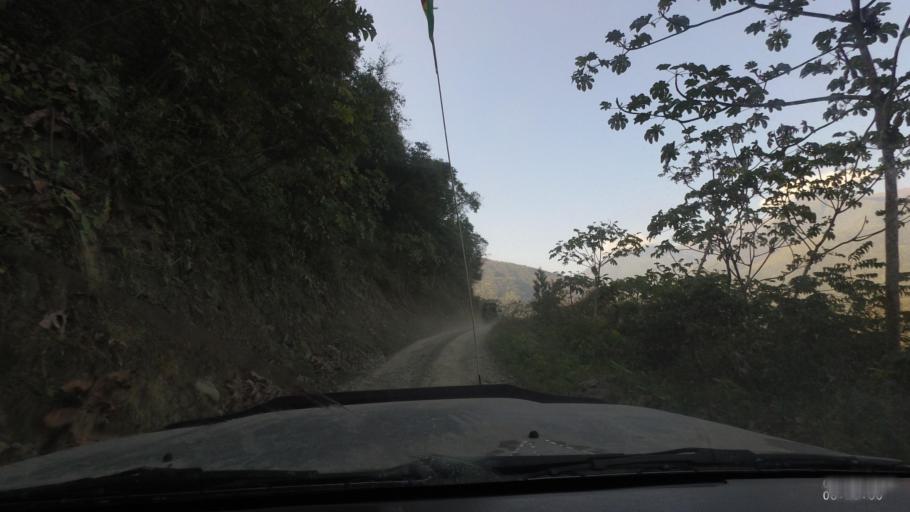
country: BO
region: La Paz
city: Quime
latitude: -16.5002
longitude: -66.7680
